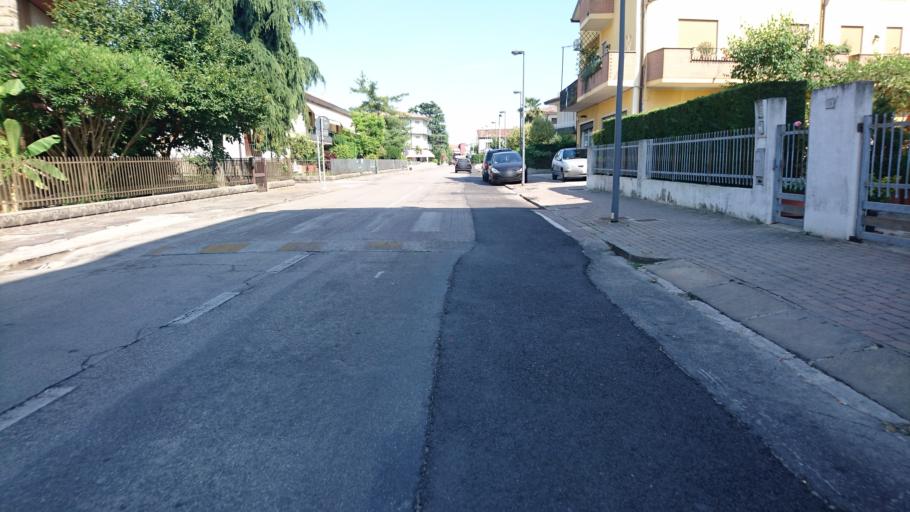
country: IT
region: Veneto
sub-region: Provincia di Padova
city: Montegrotto Terme
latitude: 45.3326
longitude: 11.7866
